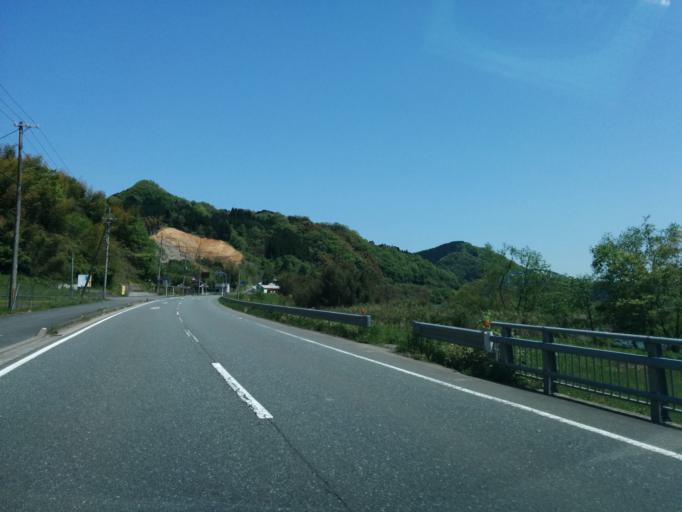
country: JP
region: Kyoto
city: Miyazu
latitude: 35.4167
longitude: 135.2025
